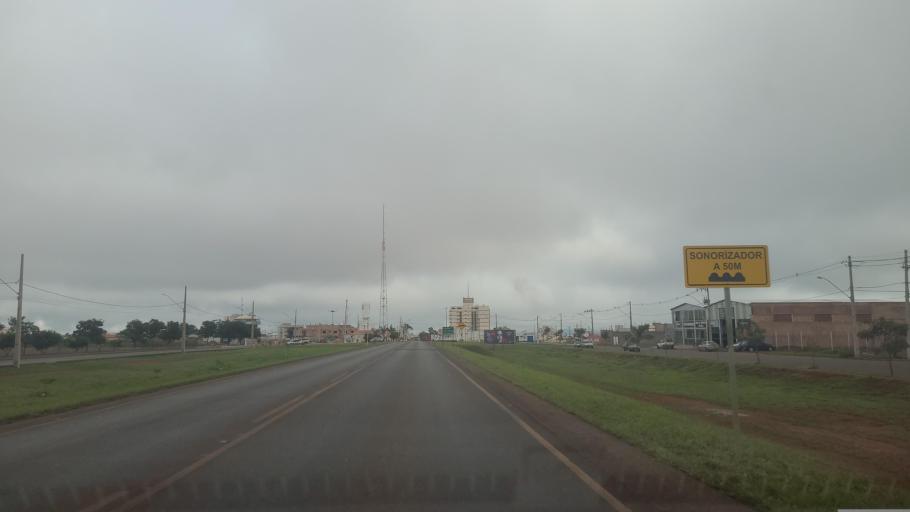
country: BR
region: Minas Gerais
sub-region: Sao Gotardo
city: Sao Gotardo
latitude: -19.2041
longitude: -46.2319
